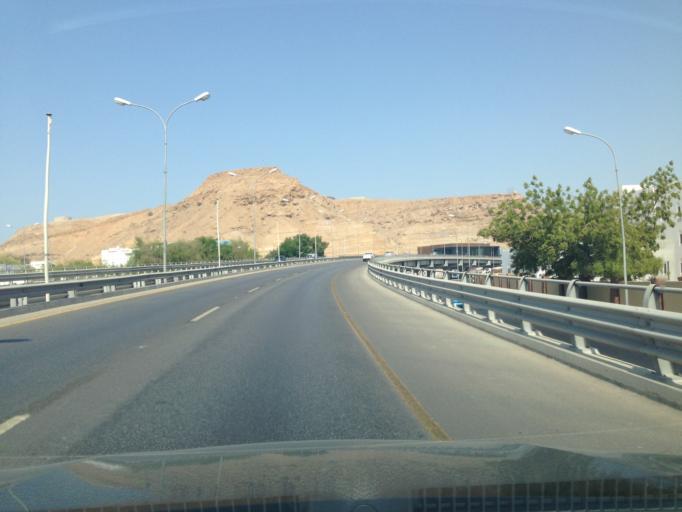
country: OM
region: Muhafazat Masqat
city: Muscat
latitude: 23.6070
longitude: 58.5072
